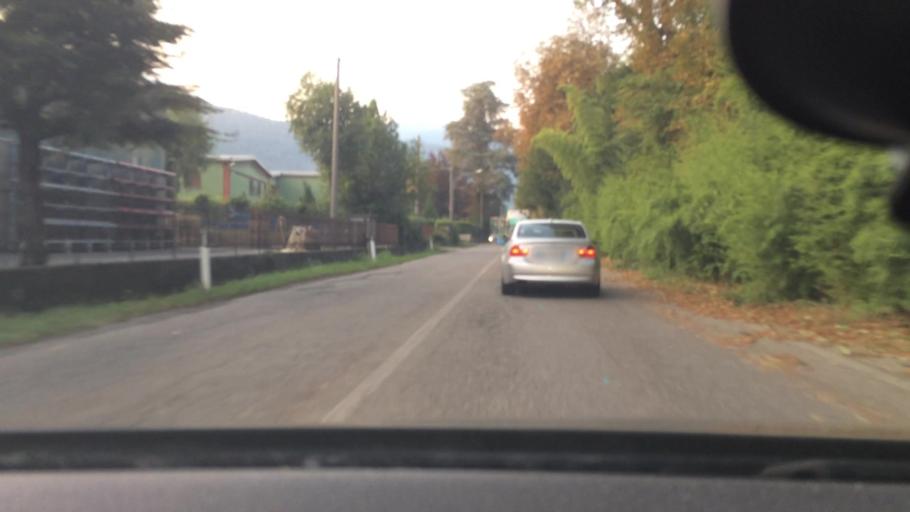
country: IT
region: Lombardy
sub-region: Provincia di Como
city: Alserio
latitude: 45.7892
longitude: 9.1973
